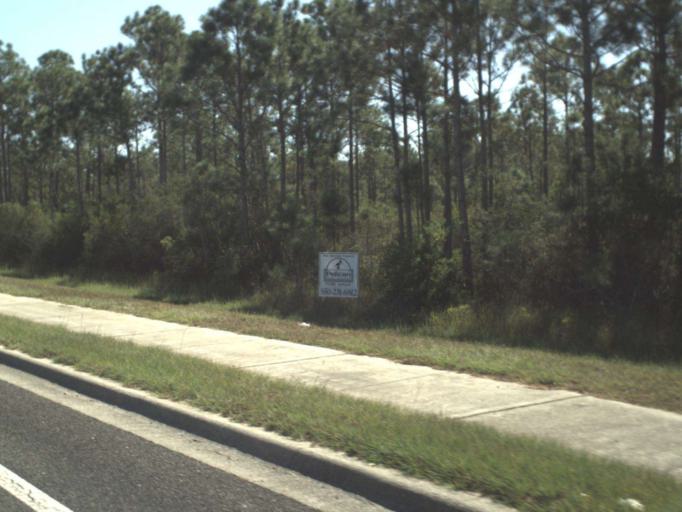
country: US
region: Florida
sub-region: Walton County
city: Seaside
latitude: 30.3738
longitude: -86.2258
